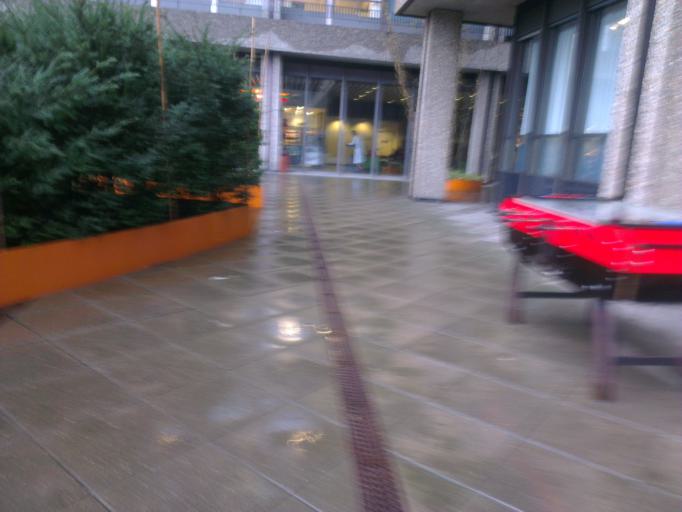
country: DK
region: Capital Region
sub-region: Kobenhavn
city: Copenhagen
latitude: 55.6962
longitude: 12.5666
